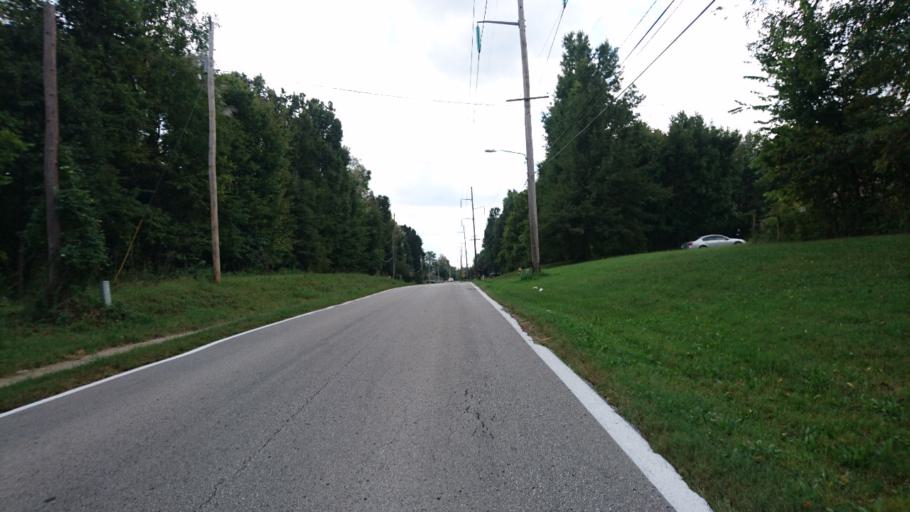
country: US
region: Missouri
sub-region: Greene County
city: Springfield
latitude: 37.2003
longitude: -93.3629
